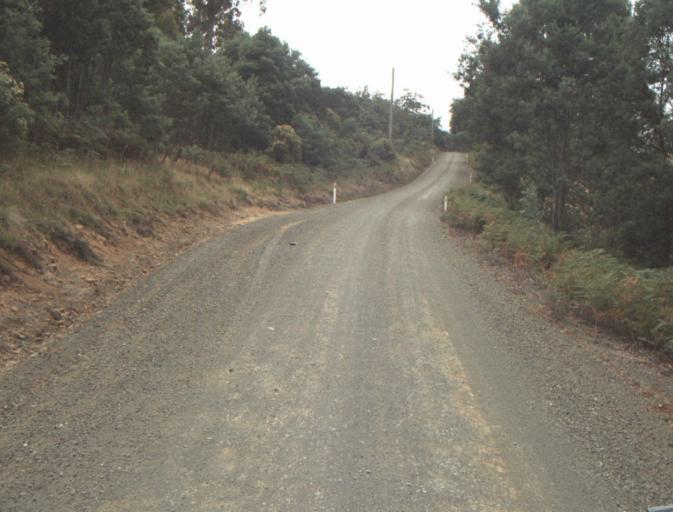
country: AU
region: Tasmania
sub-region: Northern Midlands
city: Evandale
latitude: -41.5189
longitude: 147.4134
